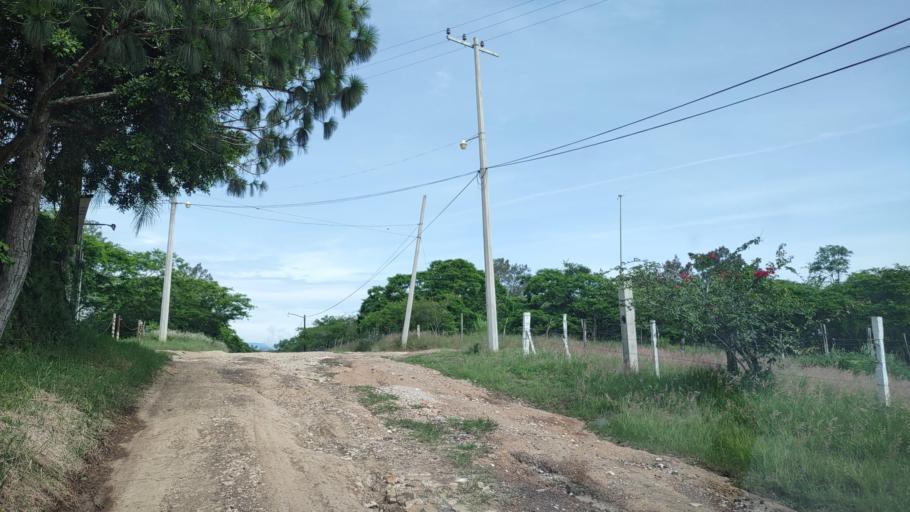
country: MX
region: Veracruz
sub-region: Emiliano Zapata
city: Dos Rios
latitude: 19.4705
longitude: -96.8279
